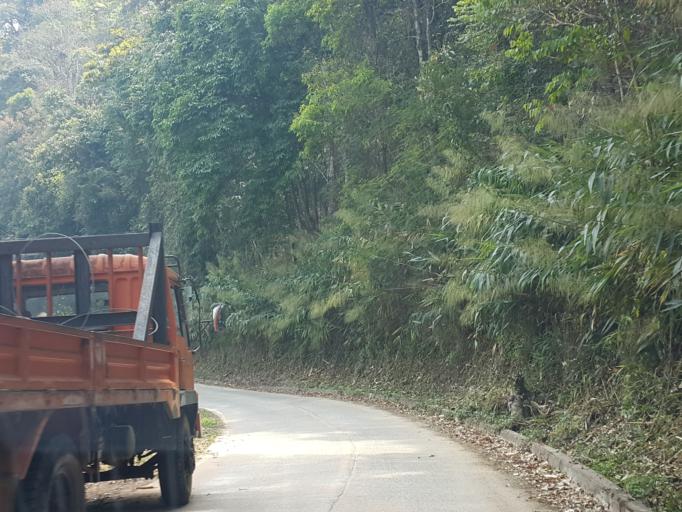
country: TH
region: Lampang
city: Mueang Pan
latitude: 18.8262
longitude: 99.4092
